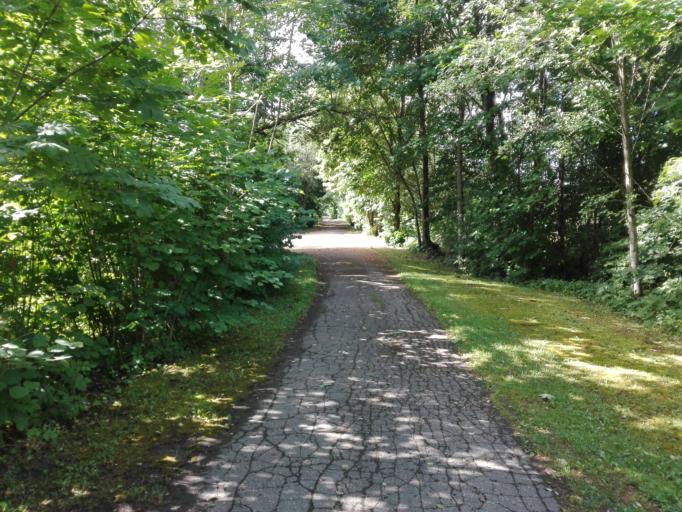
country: LT
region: Panevezys
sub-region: Birzai
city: Birzai
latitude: 56.2240
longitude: 24.7807
